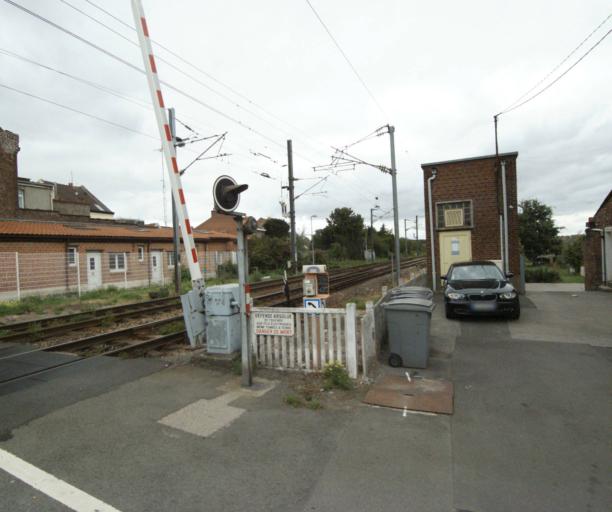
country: FR
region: Nord-Pas-de-Calais
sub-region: Departement du Nord
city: Lesquin
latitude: 50.5911
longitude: 3.1179
